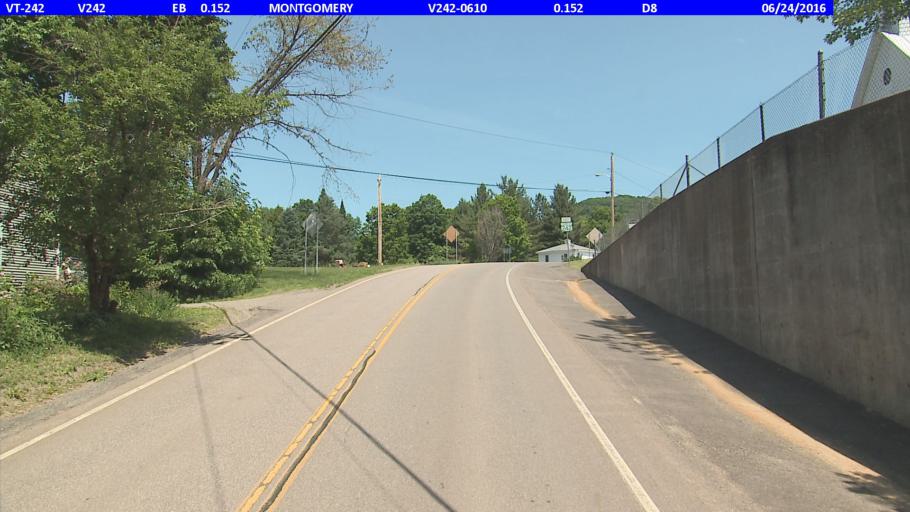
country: US
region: Vermont
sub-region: Franklin County
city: Richford
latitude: 44.8794
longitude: -72.6073
